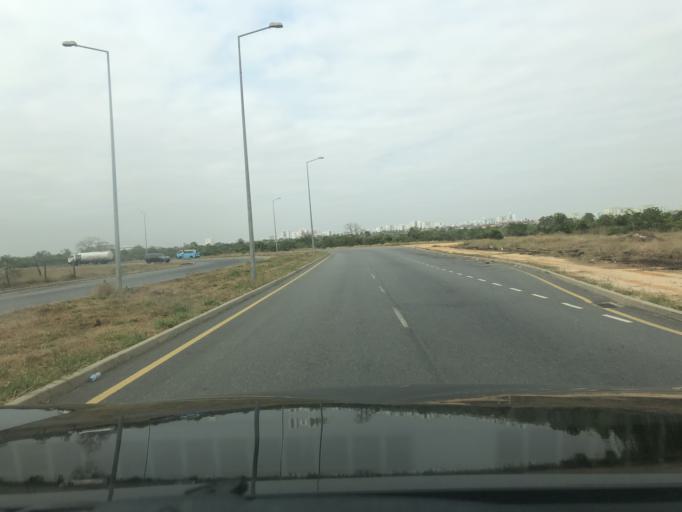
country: AO
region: Luanda
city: Luanda
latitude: -8.9748
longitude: 13.2772
